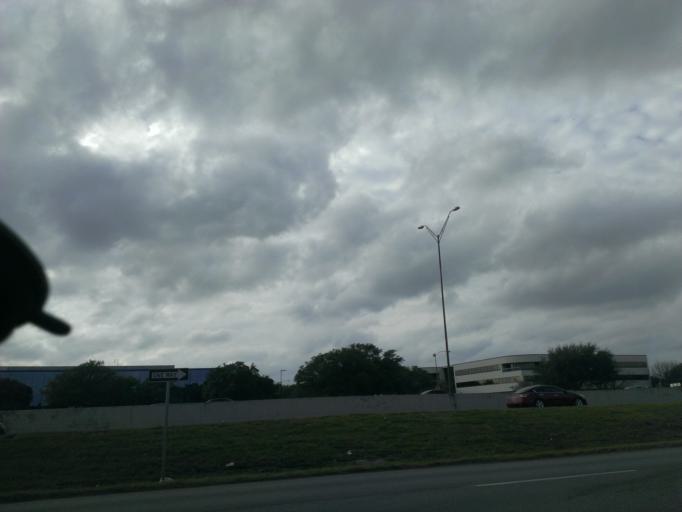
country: US
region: Texas
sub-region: Travis County
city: Wells Branch
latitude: 30.3928
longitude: -97.6712
